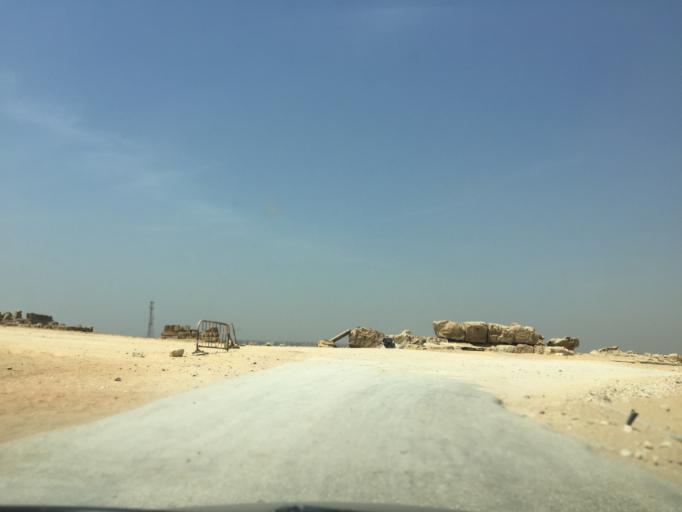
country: EG
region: Al Jizah
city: Al Jizah
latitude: 29.9777
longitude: 31.1286
